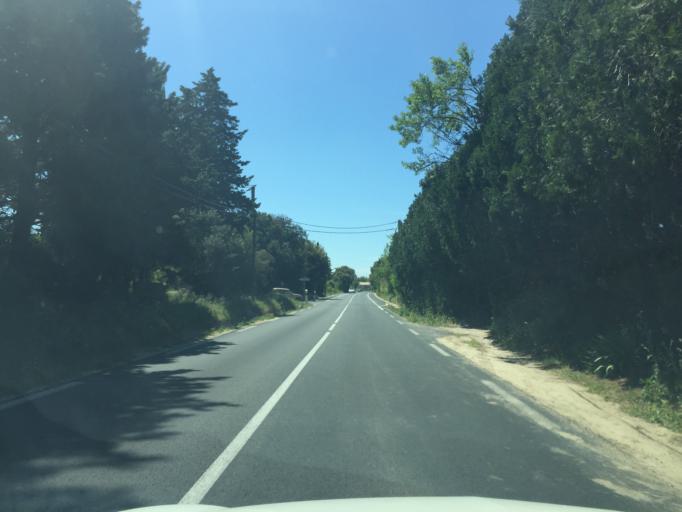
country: FR
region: Provence-Alpes-Cote d'Azur
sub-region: Departement du Vaucluse
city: Orange
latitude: 44.1128
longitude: 4.7939
